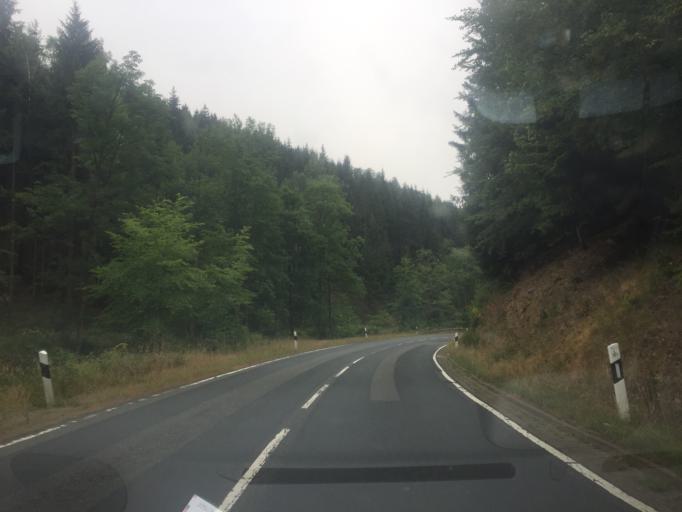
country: DE
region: Lower Saxony
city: Wieda
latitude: 51.6564
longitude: 10.5864
